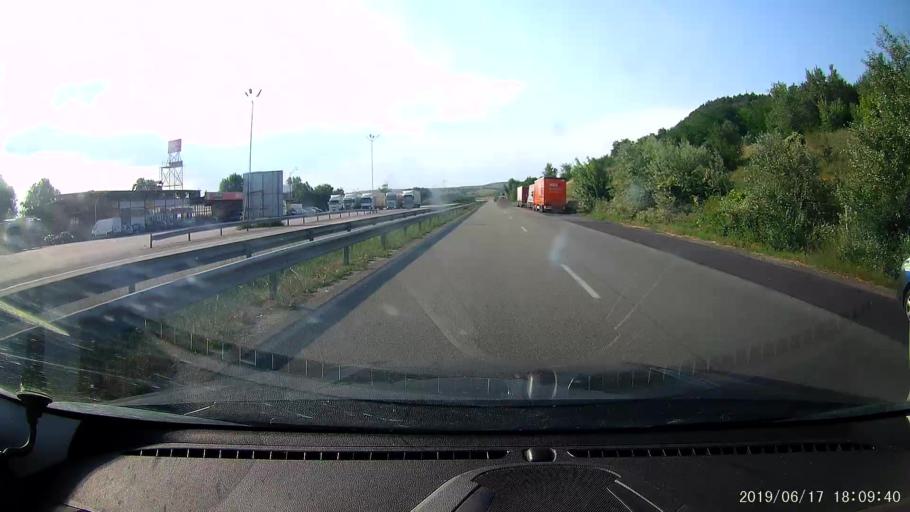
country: BG
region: Khaskovo
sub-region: Obshtina Lyubimets
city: Lyubimets
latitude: 41.8632
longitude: 26.0872
